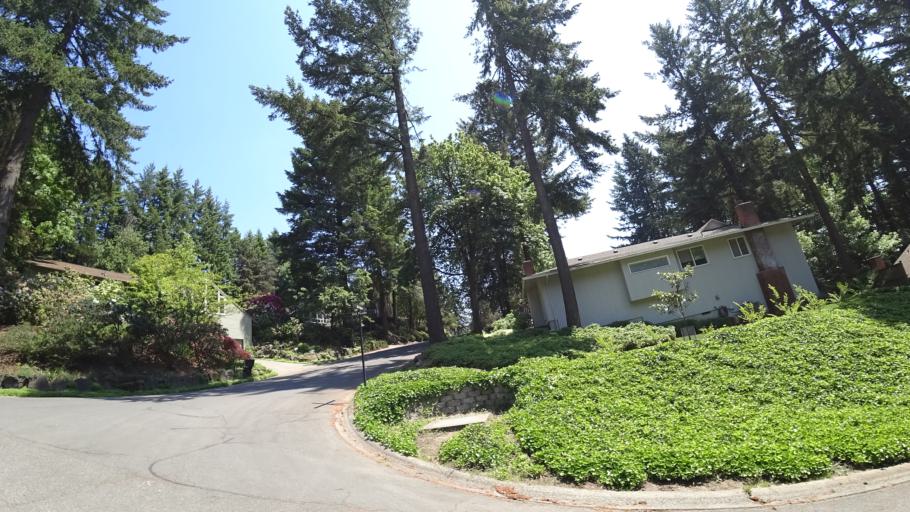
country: US
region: Oregon
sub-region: Washington County
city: Metzger
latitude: 45.4315
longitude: -122.7215
